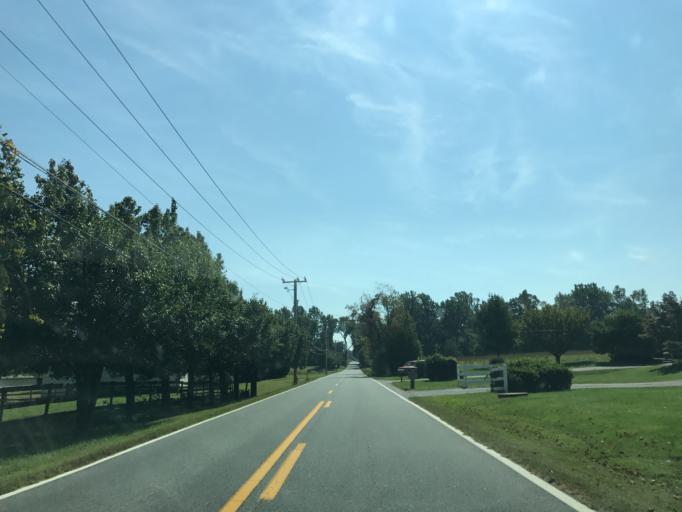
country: US
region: Maryland
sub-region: Cecil County
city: Elkton
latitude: 39.5224
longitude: -75.8151
